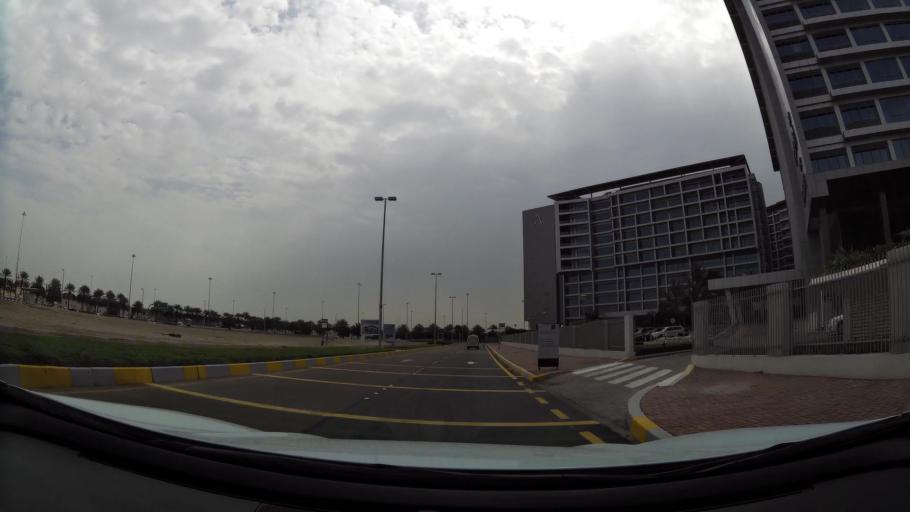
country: AE
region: Abu Dhabi
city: Abu Dhabi
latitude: 24.4248
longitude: 54.4735
